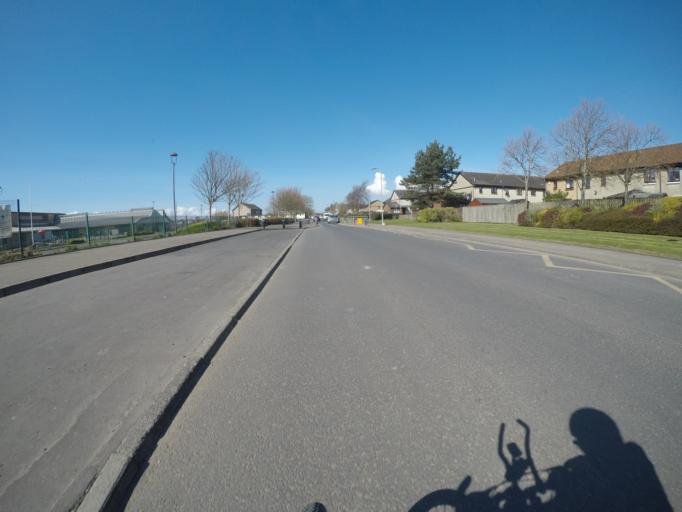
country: GB
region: Scotland
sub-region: North Ayrshire
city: Irvine
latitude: 55.6194
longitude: -4.6580
